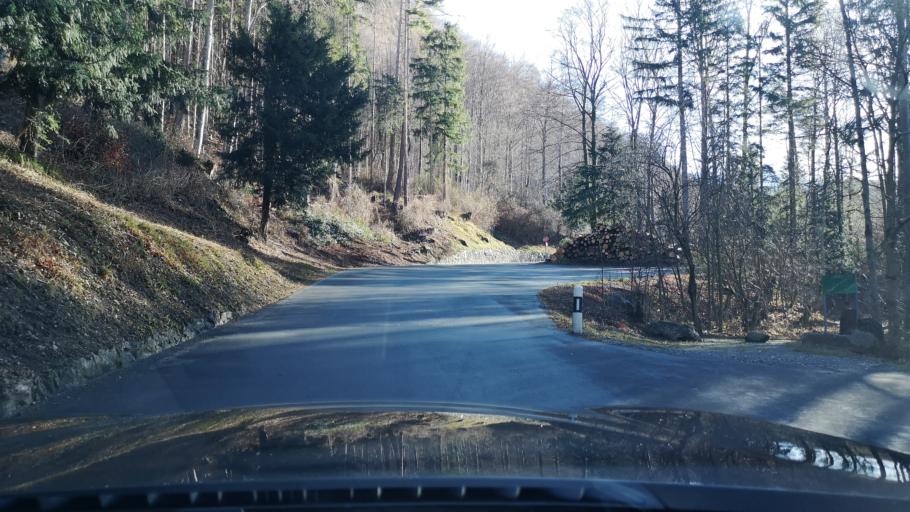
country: LI
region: Vaduz
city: Vaduz
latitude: 47.1355
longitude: 9.5280
